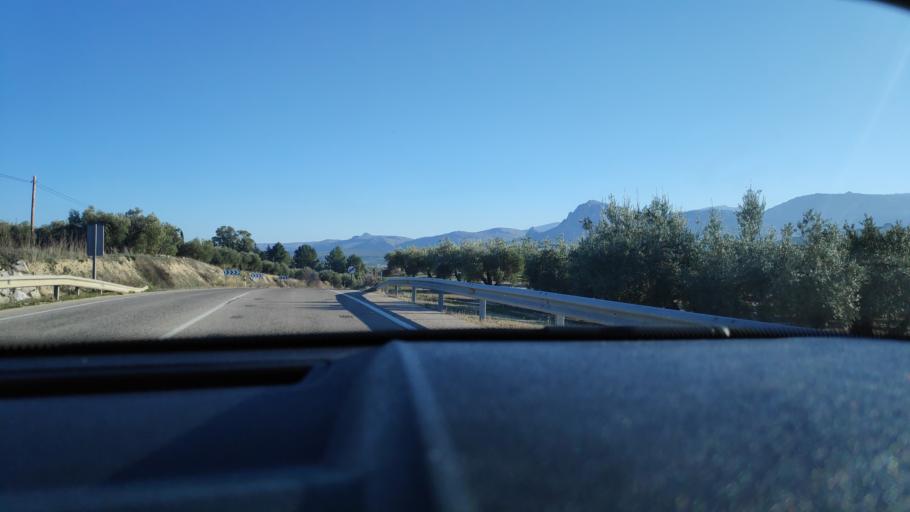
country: ES
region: Andalusia
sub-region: Province of Cordoba
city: Baena
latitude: 37.5915
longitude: -4.2971
